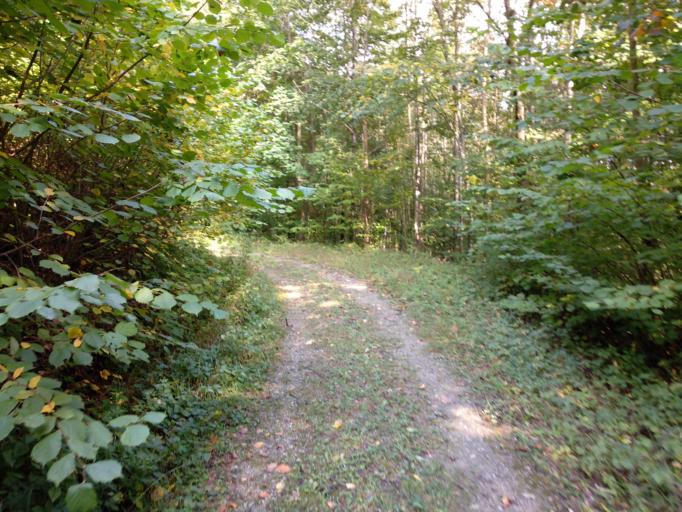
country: DE
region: North Rhine-Westphalia
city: Beverungen
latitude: 51.6402
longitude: 9.3622
